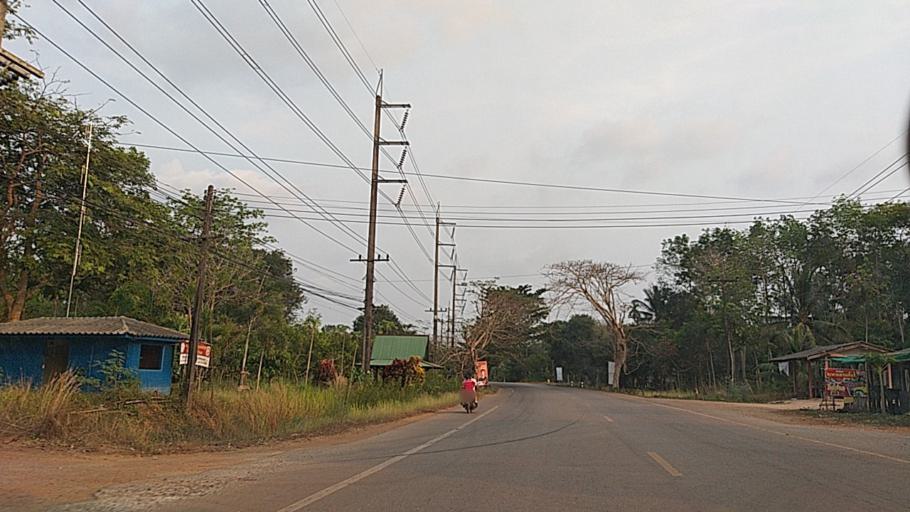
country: TH
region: Trat
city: Laem Ngop
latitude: 12.2382
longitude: 102.2965
